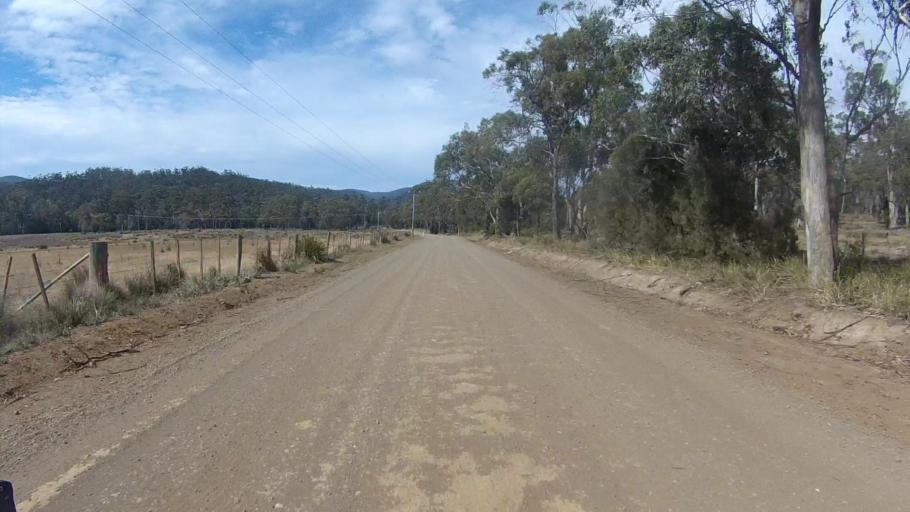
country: AU
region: Tasmania
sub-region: Sorell
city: Sorell
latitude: -42.6448
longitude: 147.9001
